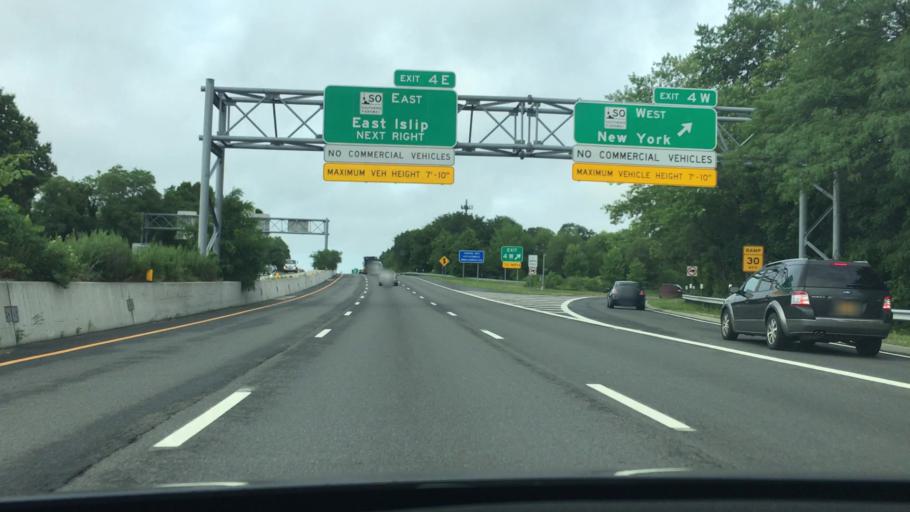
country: US
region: New York
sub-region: Nassau County
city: Plainedge
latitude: 40.7033
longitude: -73.4894
